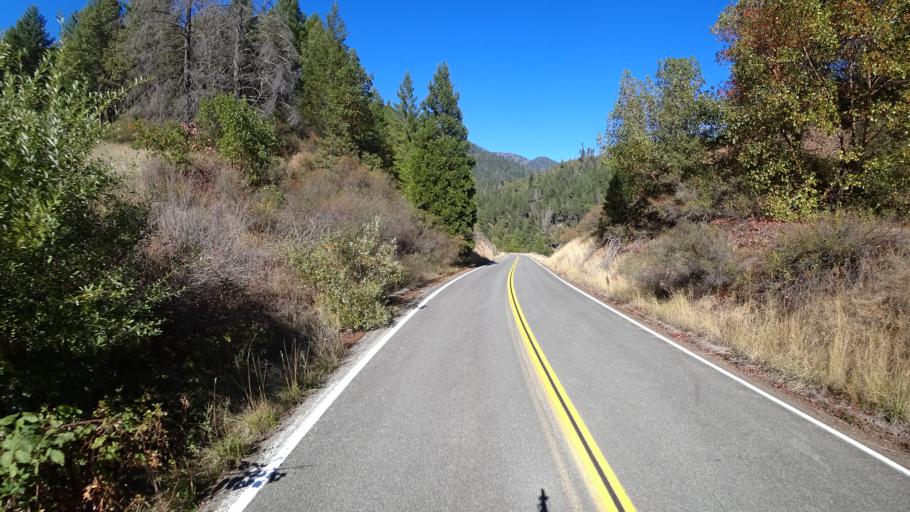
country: US
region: California
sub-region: Siskiyou County
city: Happy Camp
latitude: 41.3710
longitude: -123.4173
